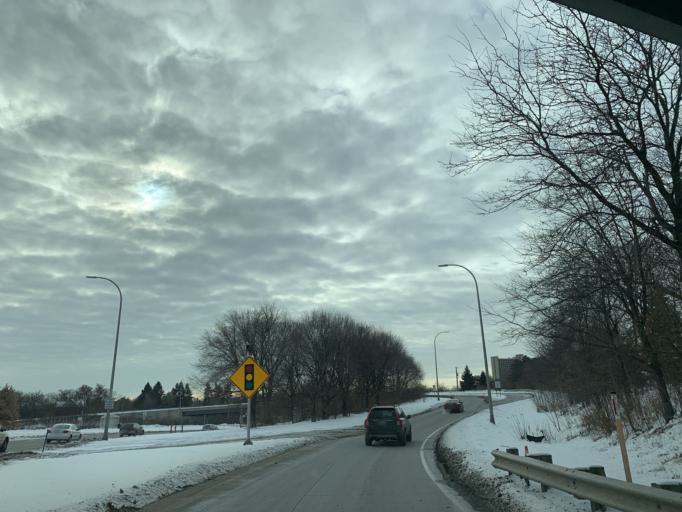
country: US
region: Minnesota
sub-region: Ramsey County
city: Lauderdale
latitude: 44.9688
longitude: -93.2230
